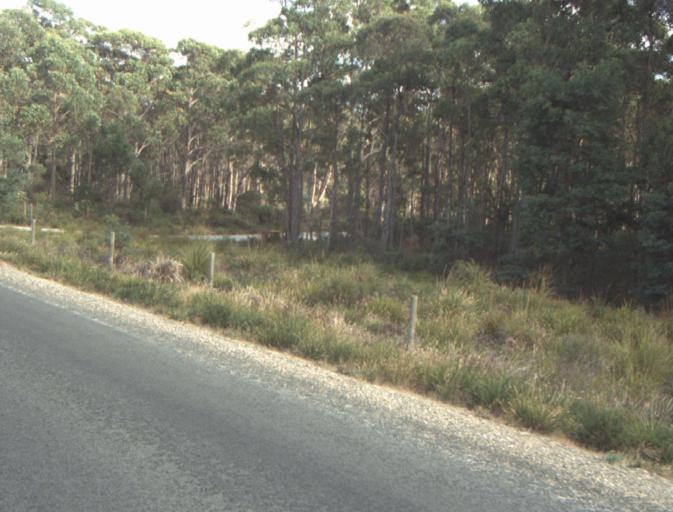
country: AU
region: Tasmania
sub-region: Dorset
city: Bridport
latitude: -41.1341
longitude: 147.2212
